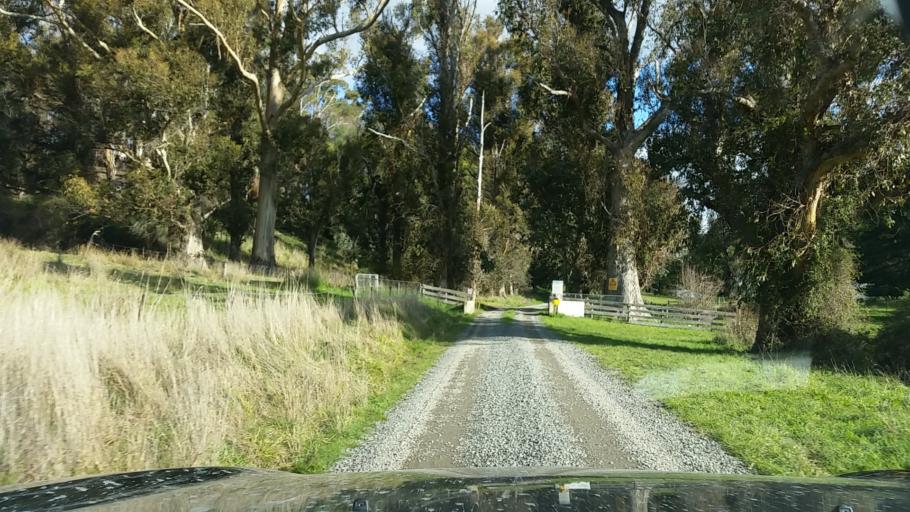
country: NZ
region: Marlborough
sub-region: Marlborough District
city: Blenheim
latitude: -41.7761
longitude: 173.8529
